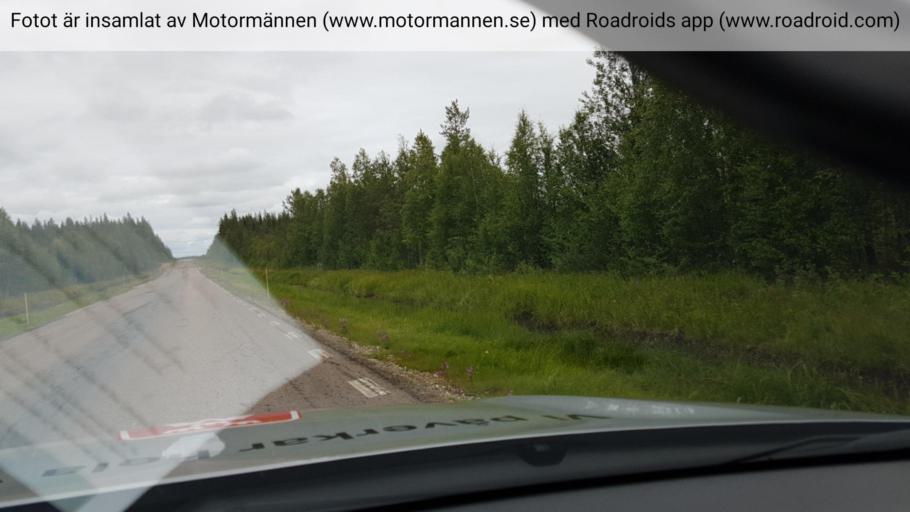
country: SE
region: Norrbotten
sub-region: Overkalix Kommun
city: OEverkalix
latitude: 67.0574
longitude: 22.3358
